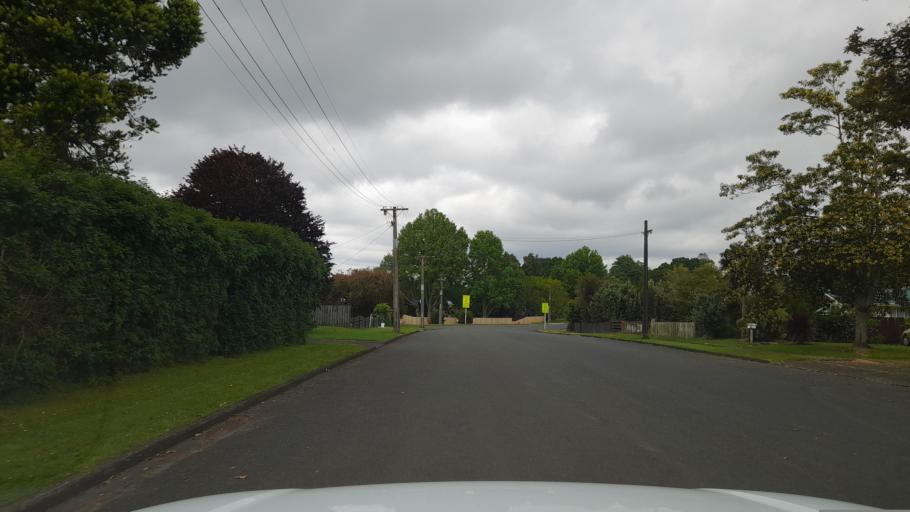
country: NZ
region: Northland
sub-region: Far North District
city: Waimate North
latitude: -35.4036
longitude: 173.7949
